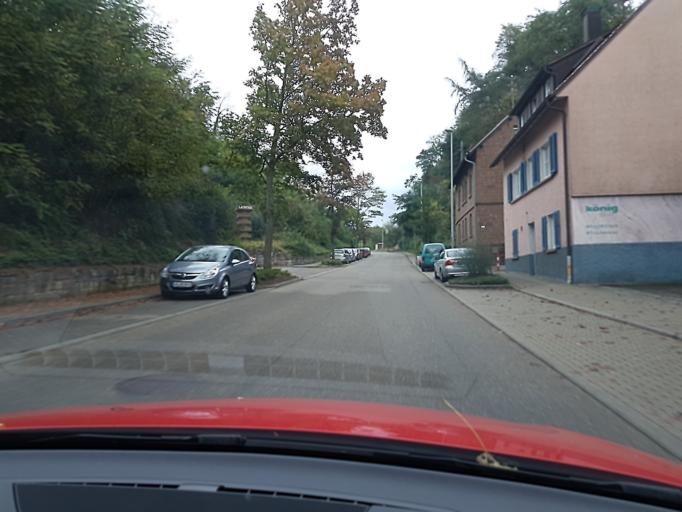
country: DE
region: Baden-Wuerttemberg
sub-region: Karlsruhe Region
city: Maulbronn
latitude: 48.9999
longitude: 8.8194
